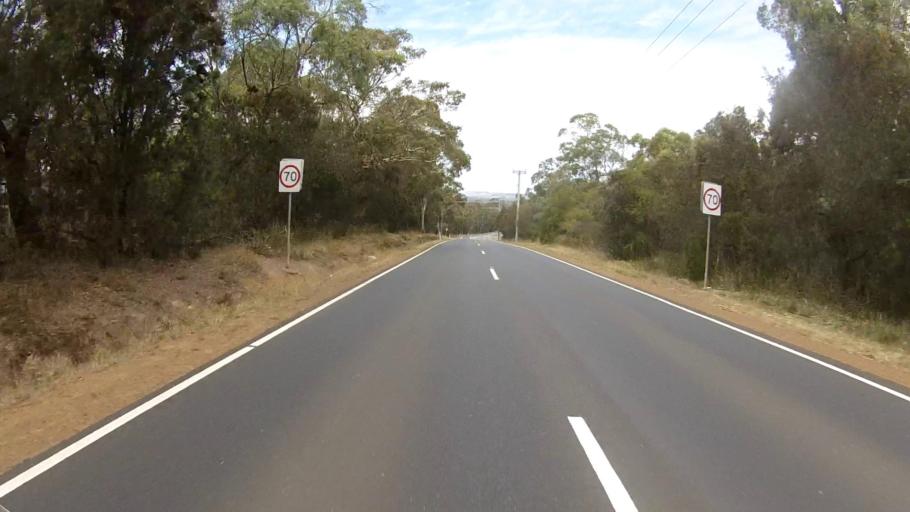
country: AU
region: Tasmania
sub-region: Clarence
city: Acton Park
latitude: -42.8825
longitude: 147.4825
